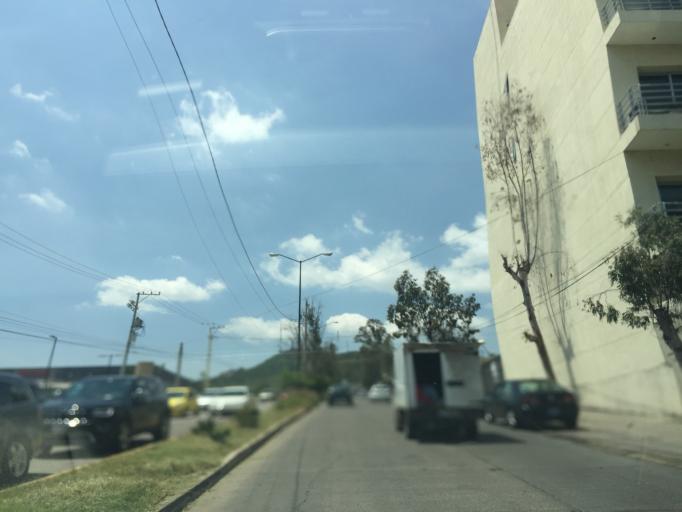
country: MX
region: Guanajuato
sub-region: Leon
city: La Ermita
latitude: 21.1581
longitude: -101.7020
